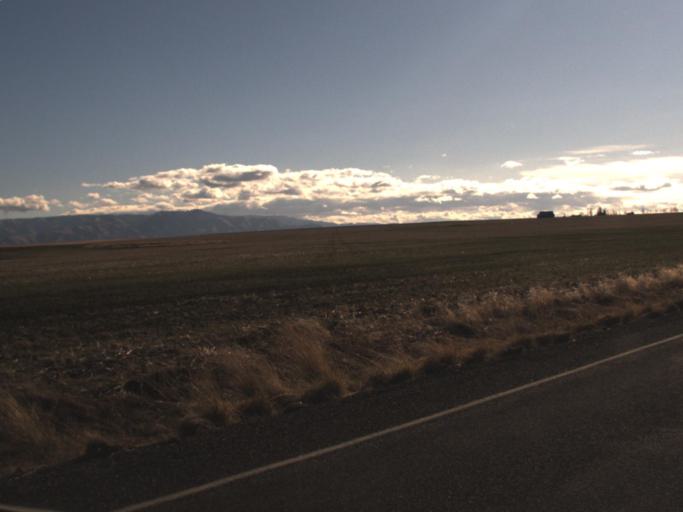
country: US
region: Washington
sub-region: Asotin County
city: Asotin
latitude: 46.2234
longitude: -117.0703
